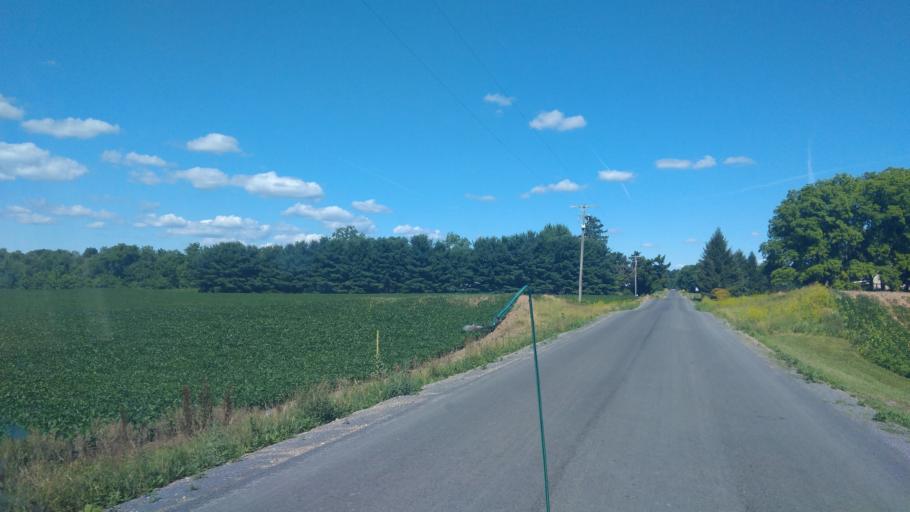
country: US
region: New York
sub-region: Wayne County
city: Clyde
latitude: 43.0262
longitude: -76.8916
